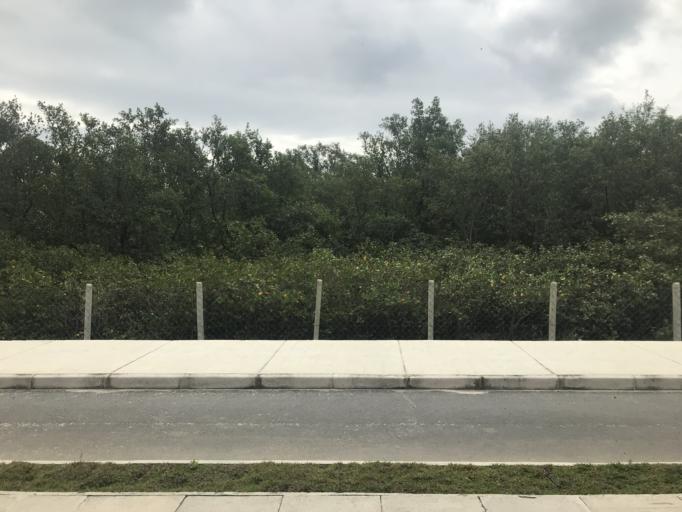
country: BR
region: Santa Catarina
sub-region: Florianopolis
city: Costeira do Pirajubae
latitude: -27.6535
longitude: -48.5242
